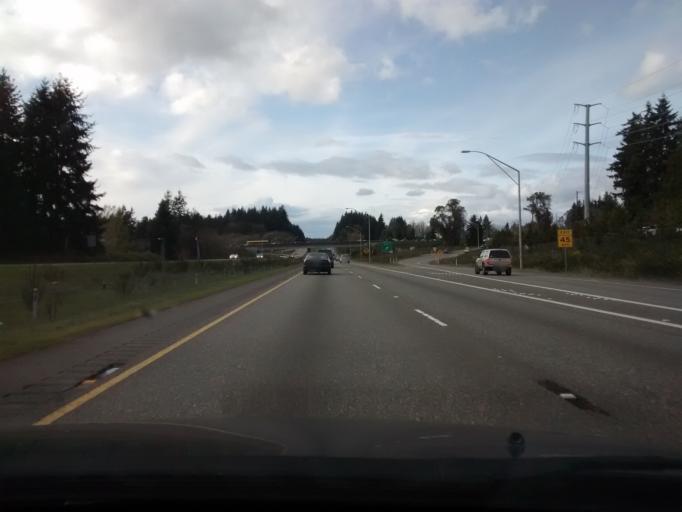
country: US
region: Washington
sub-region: Pierce County
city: Gig Harbor
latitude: 47.3181
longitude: -122.5876
